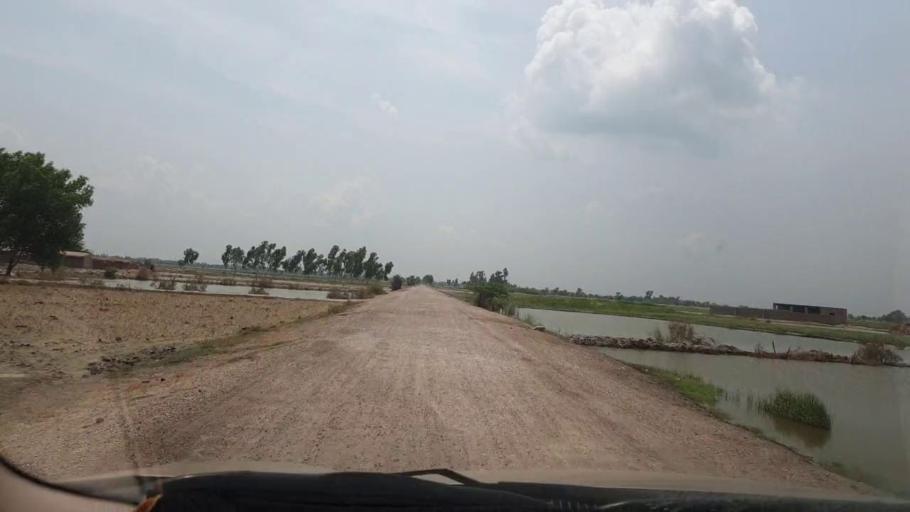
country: PK
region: Sindh
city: Larkana
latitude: 27.6204
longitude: 68.1449
